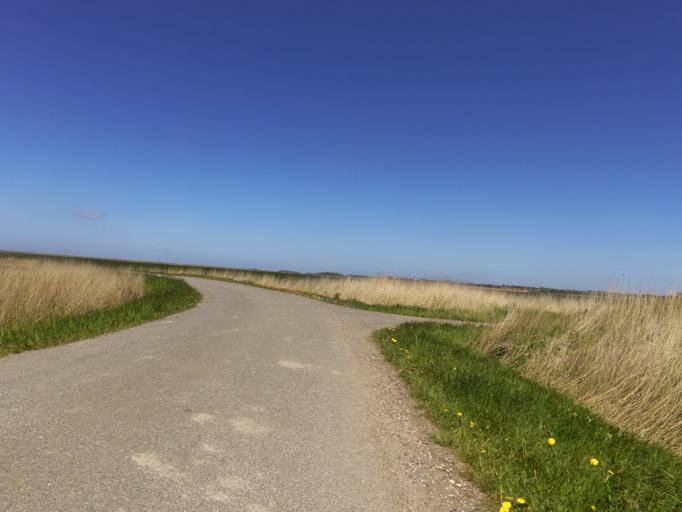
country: DK
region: South Denmark
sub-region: Tonder Kommune
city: Sherrebek
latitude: 55.2377
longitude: 8.6952
